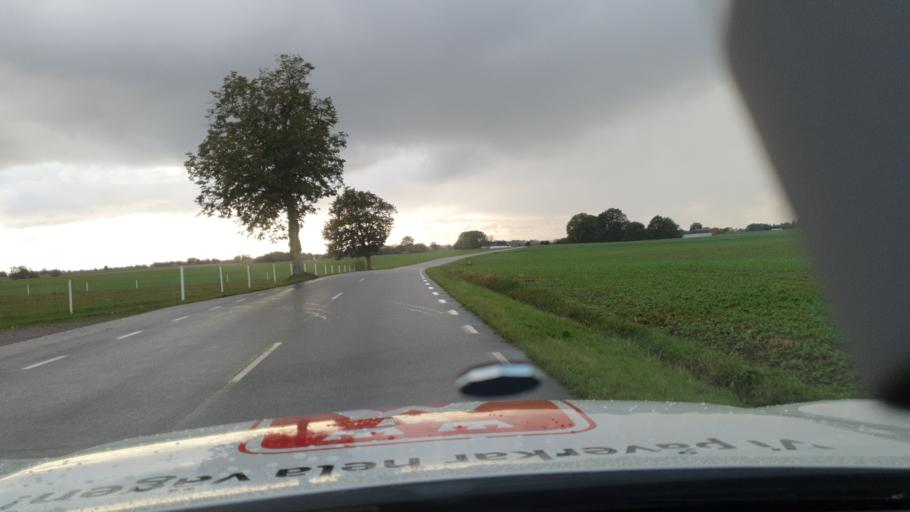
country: SE
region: Skane
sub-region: Trelleborgs Kommun
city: Anderslov
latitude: 55.4120
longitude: 13.2793
